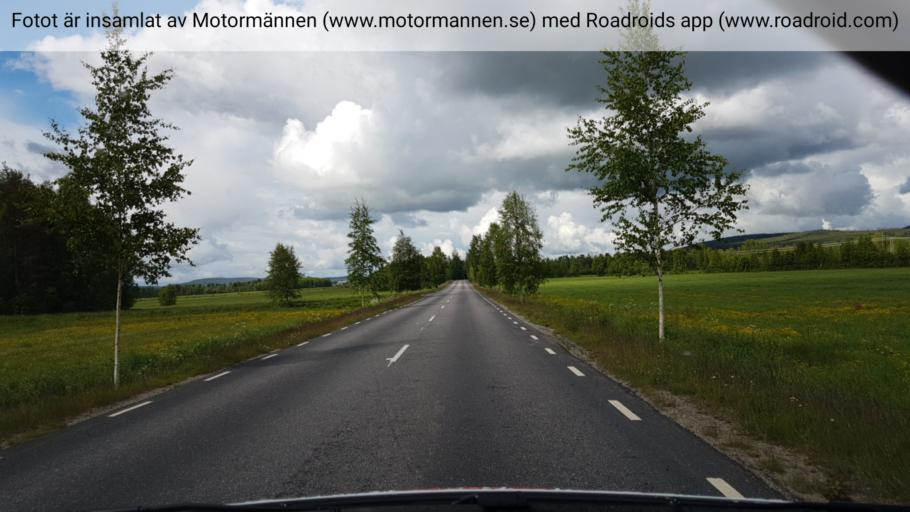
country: SE
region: Vaesterbotten
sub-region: Vannas Kommun
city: Vannasby
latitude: 63.8814
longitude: 19.8900
